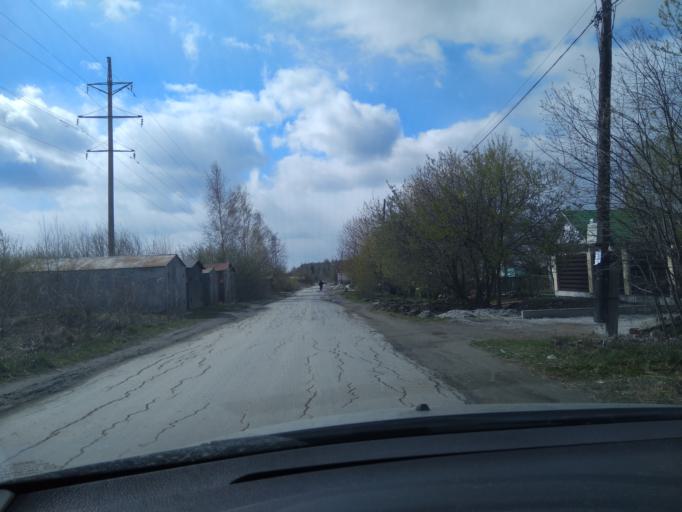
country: RU
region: Sverdlovsk
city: Sredneuralsk
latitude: 56.9782
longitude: 60.4752
